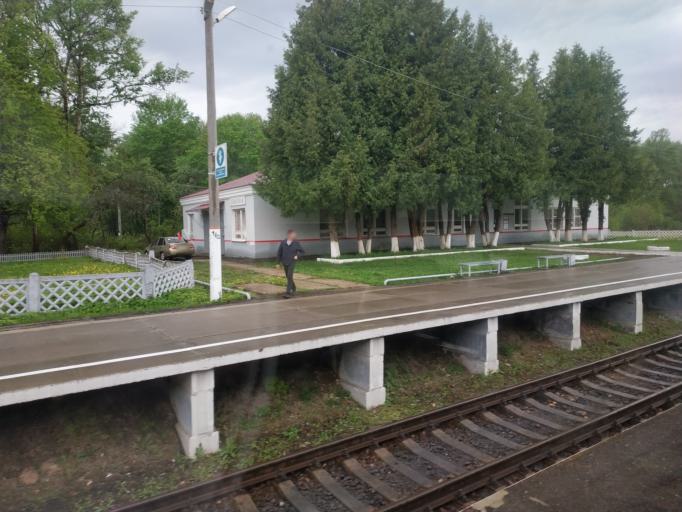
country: RU
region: Kaluga
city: Baryatino
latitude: 54.3535
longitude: 34.3195
